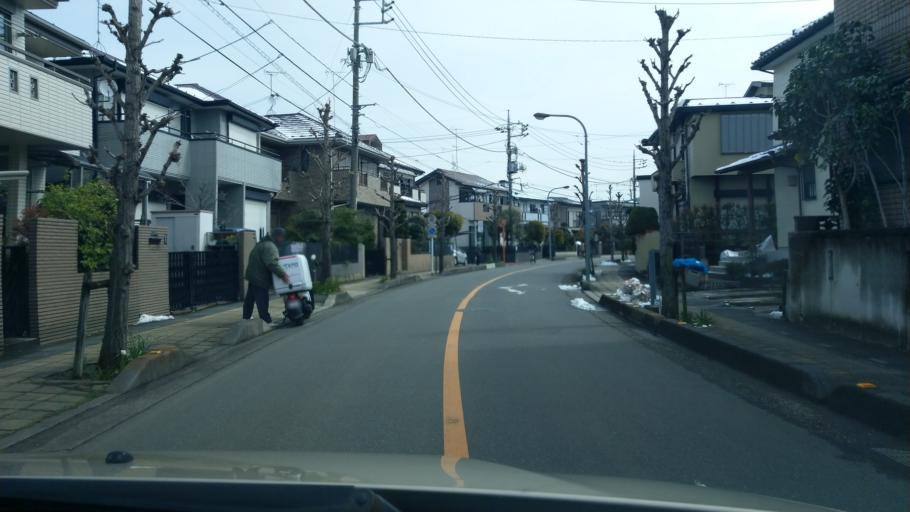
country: JP
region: Saitama
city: Yono
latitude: 35.9094
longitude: 139.5742
